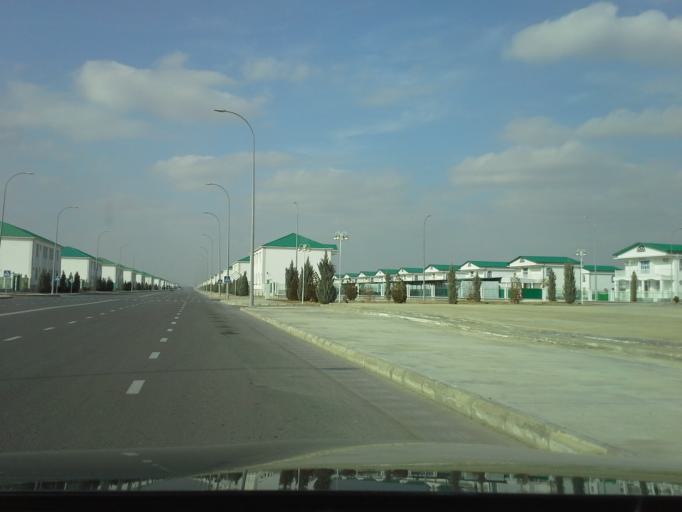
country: TM
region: Ahal
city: Abadan
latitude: 38.0771
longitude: 58.2812
